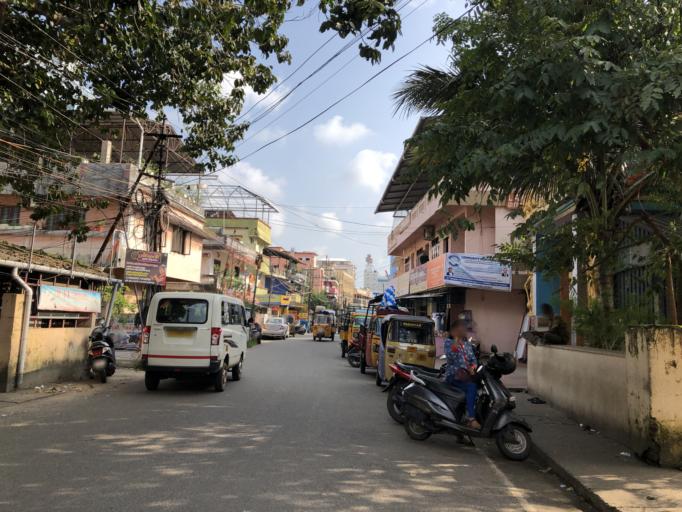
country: IN
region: Kerala
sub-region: Ernakulam
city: Cochin
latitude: 9.9799
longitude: 76.2812
